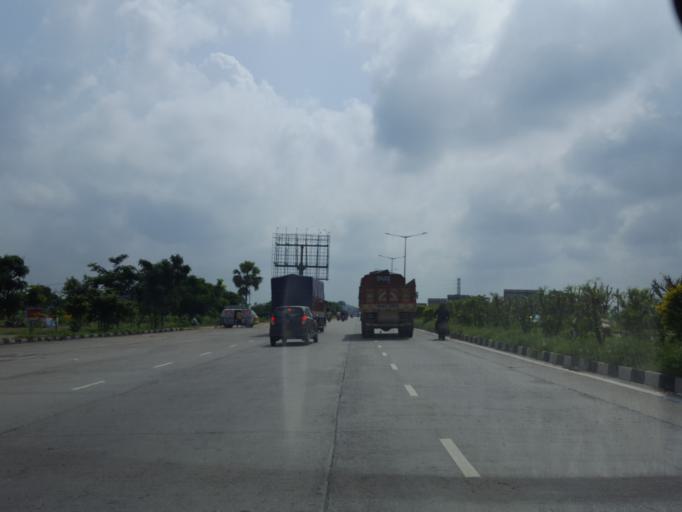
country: IN
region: Telangana
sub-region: Nalgonda
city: Bhongir
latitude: 17.2322
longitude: 78.9626
